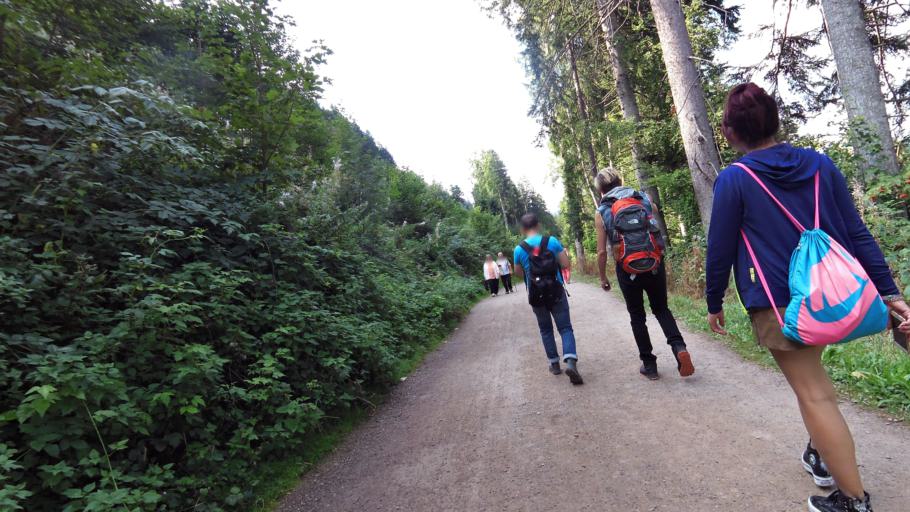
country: DE
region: Baden-Wuerttemberg
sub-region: Freiburg Region
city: Titisee-Neustadt
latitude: 47.8948
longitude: 8.1554
